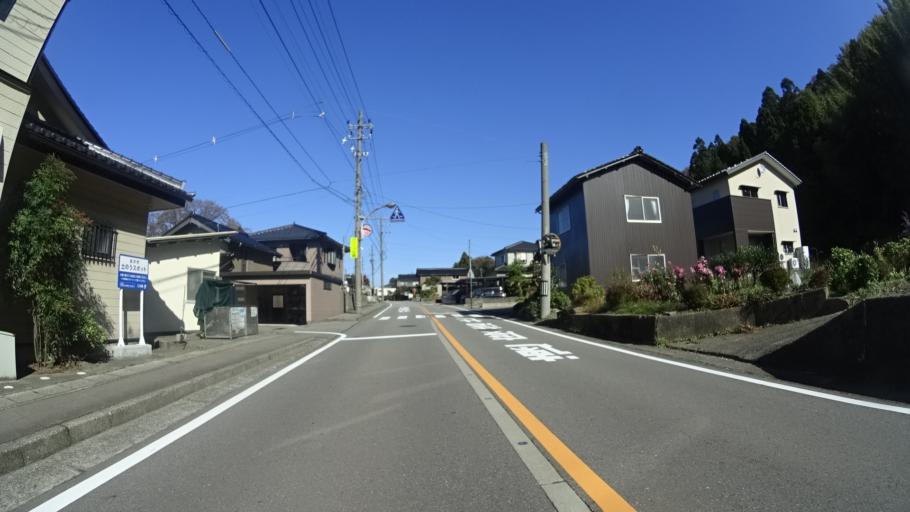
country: JP
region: Ishikawa
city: Nonoichi
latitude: 36.4973
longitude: 136.6216
